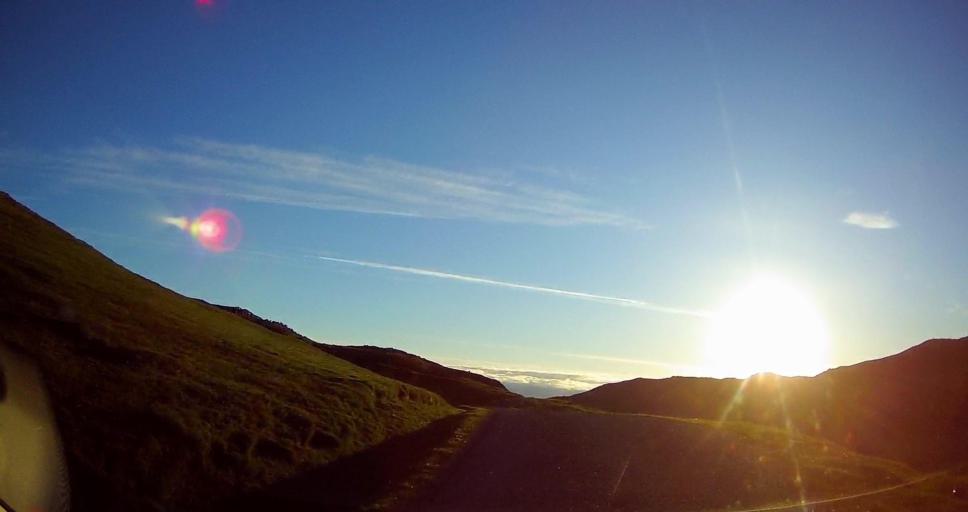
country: GB
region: Scotland
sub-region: Shetland Islands
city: Lerwick
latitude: 60.4487
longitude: -1.4178
